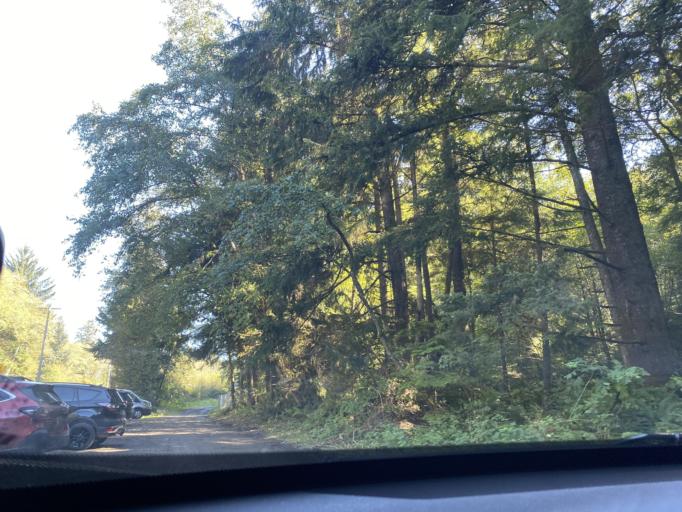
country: US
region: Washington
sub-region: Clallam County
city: Forks
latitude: 47.8981
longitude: -124.6229
